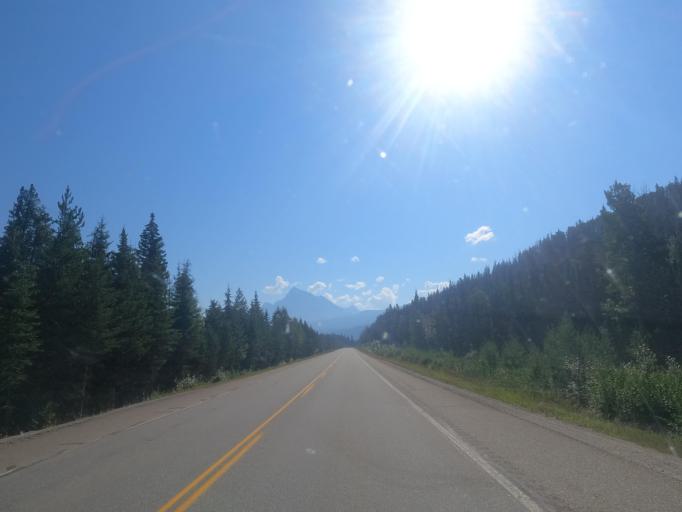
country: CA
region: Alberta
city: Jasper Park Lodge
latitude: 52.8591
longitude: -118.6364
